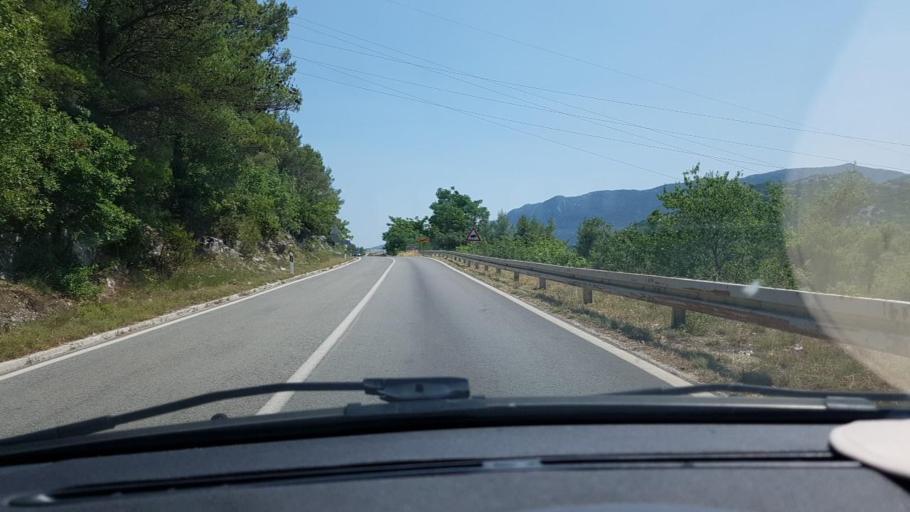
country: HR
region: Splitsko-Dalmatinska
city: Vrgorac
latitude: 43.1984
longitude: 17.3766
